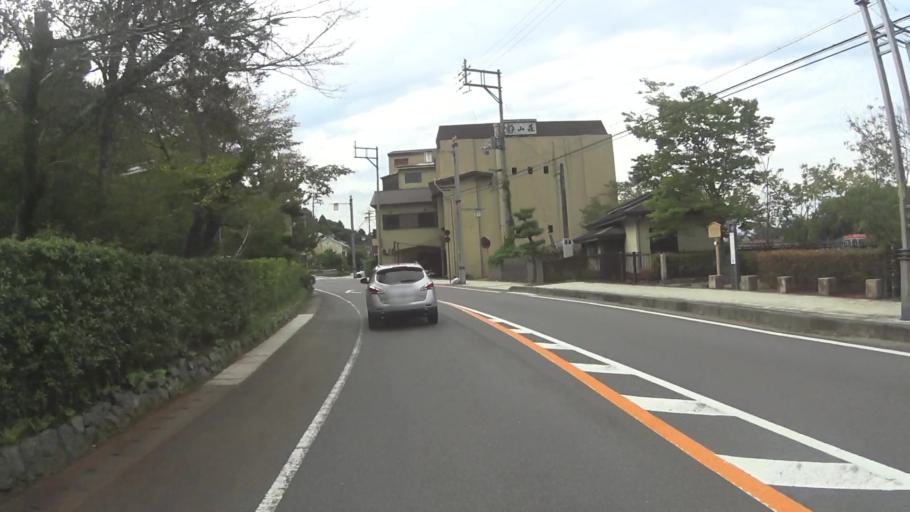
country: JP
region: Kyoto
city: Uji
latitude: 34.8868
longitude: 135.8124
